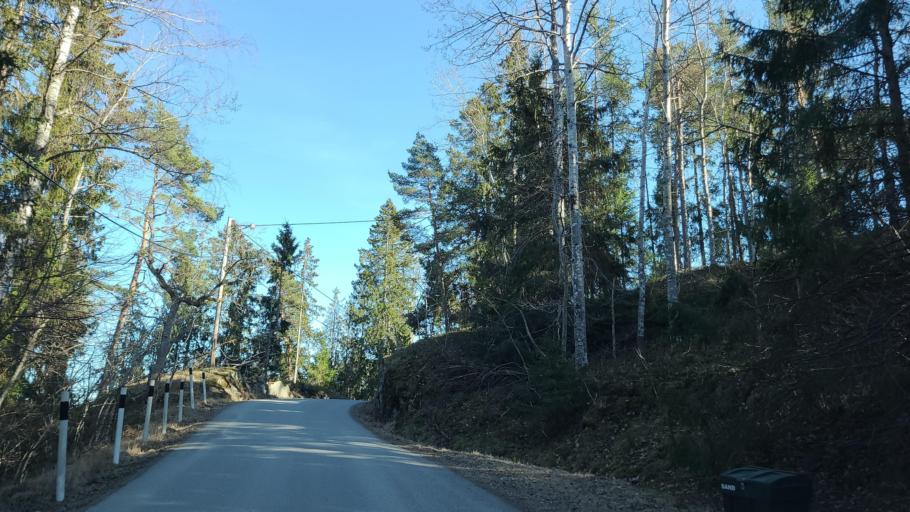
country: SE
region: Stockholm
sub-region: Varmdo Kommun
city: Holo
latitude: 59.3624
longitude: 18.6556
